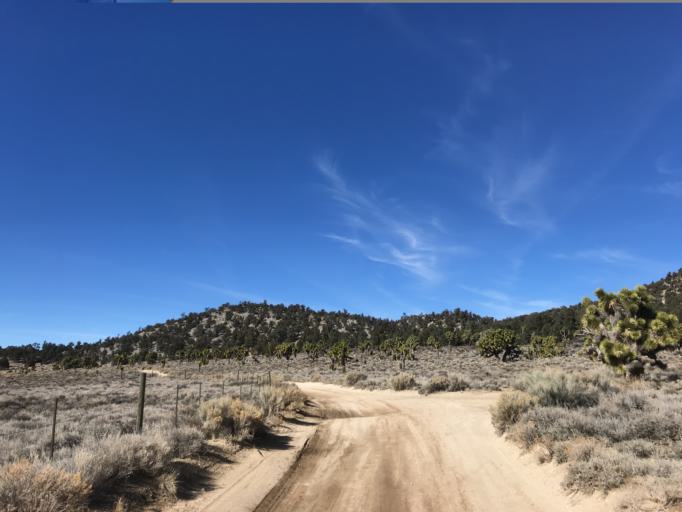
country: US
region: California
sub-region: San Bernardino County
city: Big Bear City
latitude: 34.2548
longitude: -116.7107
